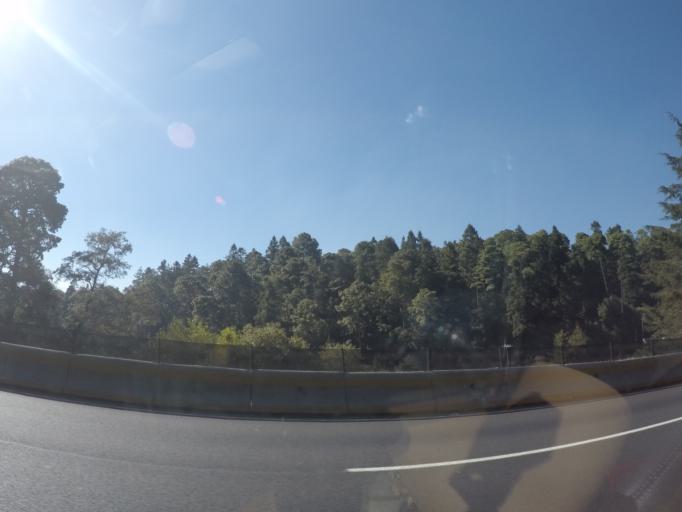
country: MX
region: Mexico City
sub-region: Cuajimalpa de Morelos
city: San Lorenzo Acopilco
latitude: 19.3291
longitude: -99.3162
